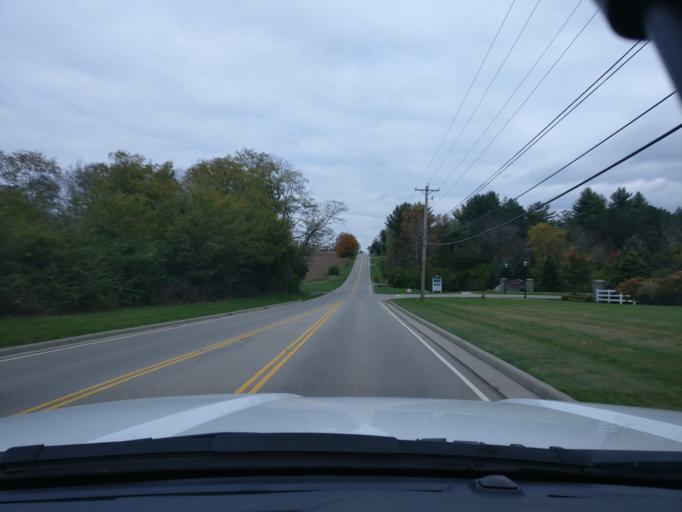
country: US
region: Ohio
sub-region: Warren County
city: Hunter
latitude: 39.4641
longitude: -84.2969
